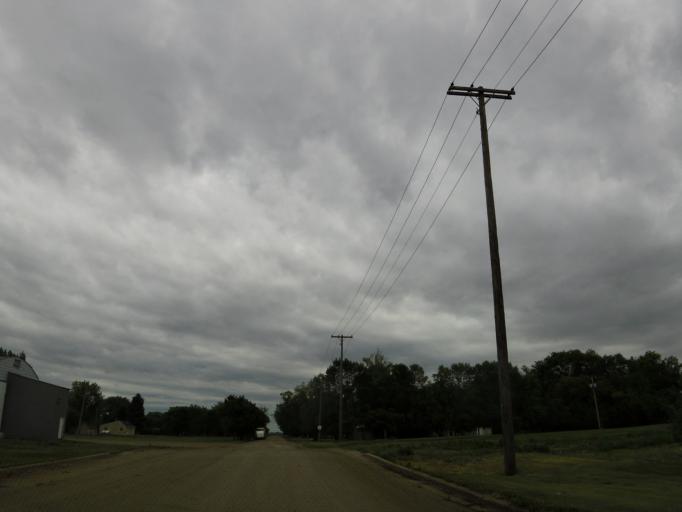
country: US
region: North Dakota
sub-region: Walsh County
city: Grafton
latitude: 48.6161
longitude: -97.4476
